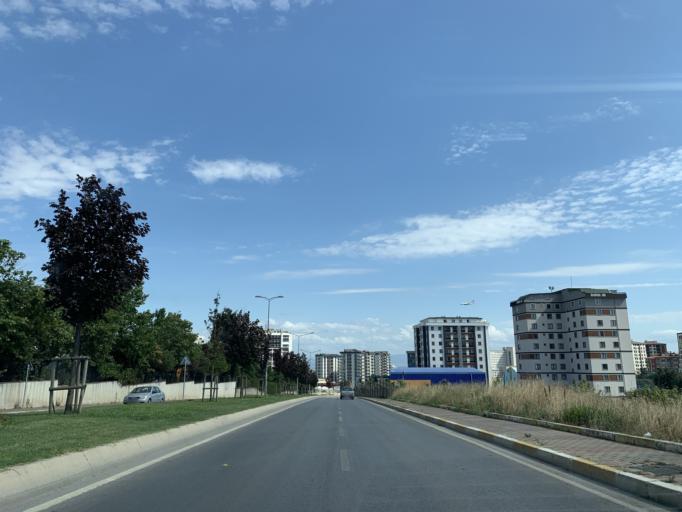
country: TR
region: Istanbul
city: Pendik
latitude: 40.8946
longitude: 29.2615
